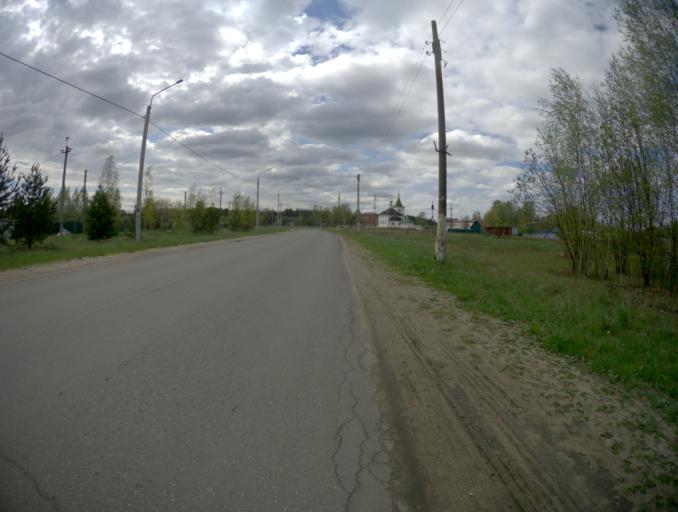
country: RU
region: Vladimir
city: Golovino
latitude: 55.9502
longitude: 40.4446
